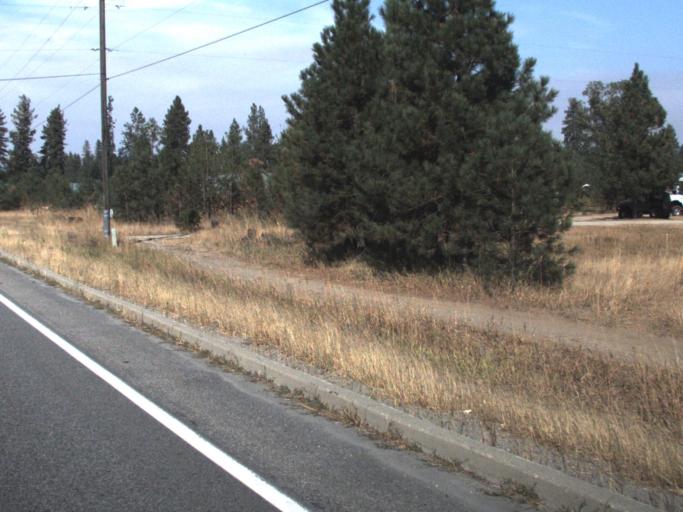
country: US
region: Washington
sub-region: Spokane County
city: Deer Park
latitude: 48.0186
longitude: -117.3496
